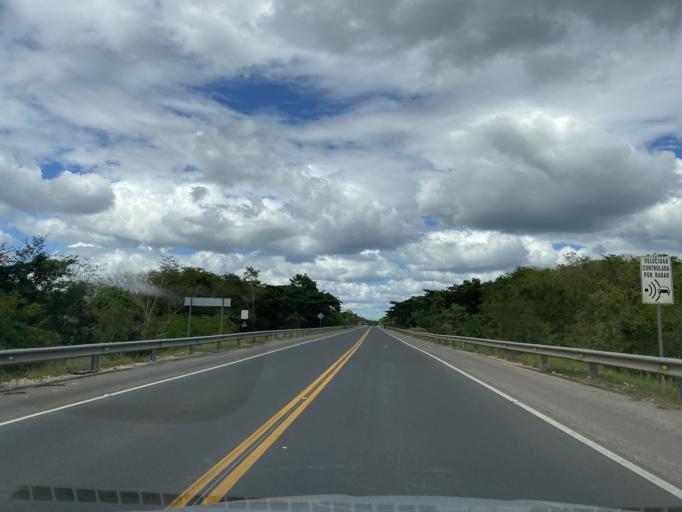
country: DO
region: Santo Domingo
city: Guerra
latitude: 18.5846
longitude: -69.7690
